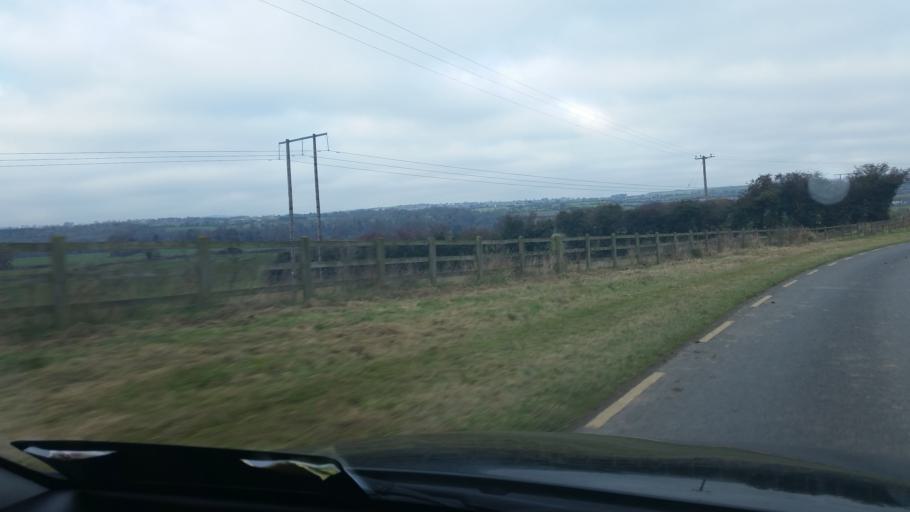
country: IE
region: Leinster
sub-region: Lu
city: Tullyallen
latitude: 53.7125
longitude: -6.4137
